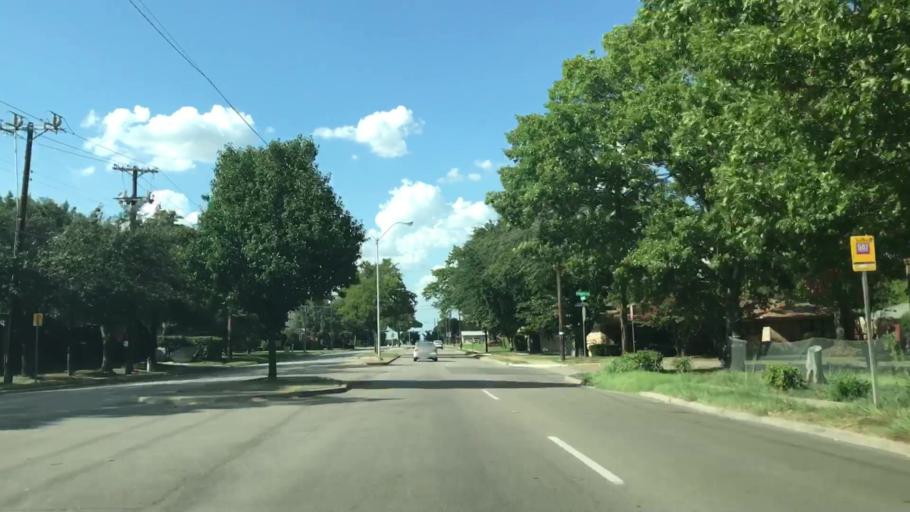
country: US
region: Texas
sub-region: Dallas County
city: Irving
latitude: 32.8508
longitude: -96.9504
